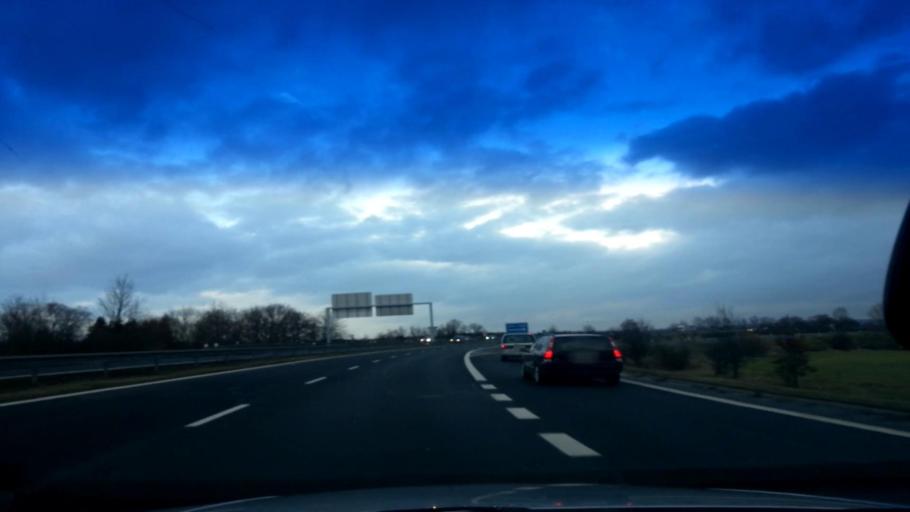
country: CZ
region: Karlovarsky
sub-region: Okres Cheb
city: Frantiskovy Lazne
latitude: 50.1015
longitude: 12.3656
